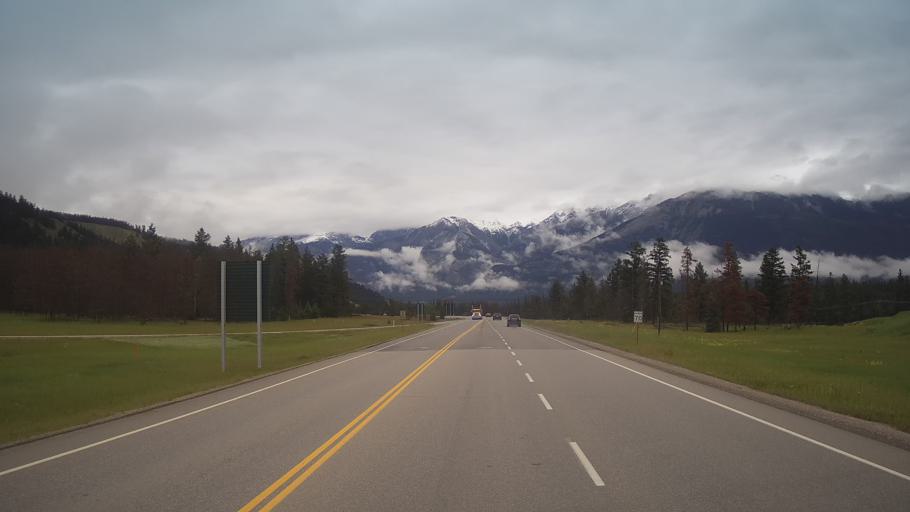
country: CA
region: Alberta
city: Jasper Park Lodge
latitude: 52.8957
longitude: -118.0694
